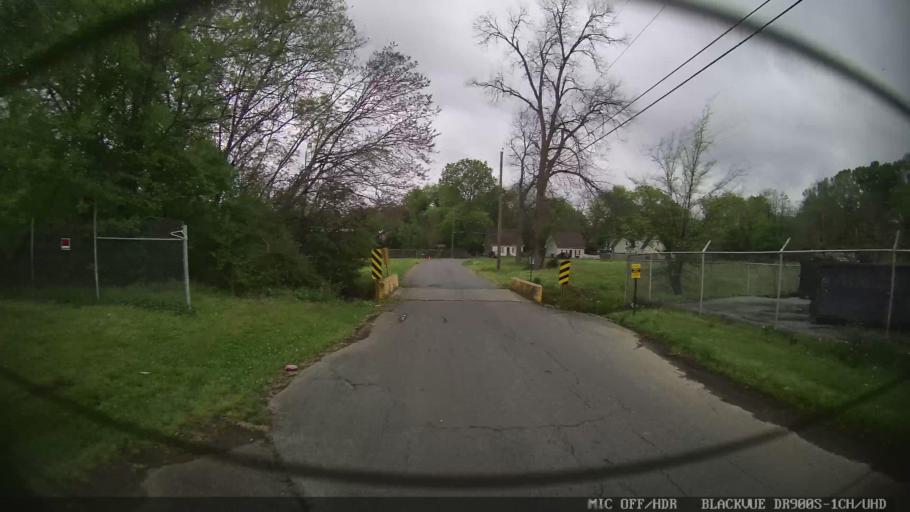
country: US
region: Georgia
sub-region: Bartow County
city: Cartersville
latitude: 34.1724
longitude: -84.7984
